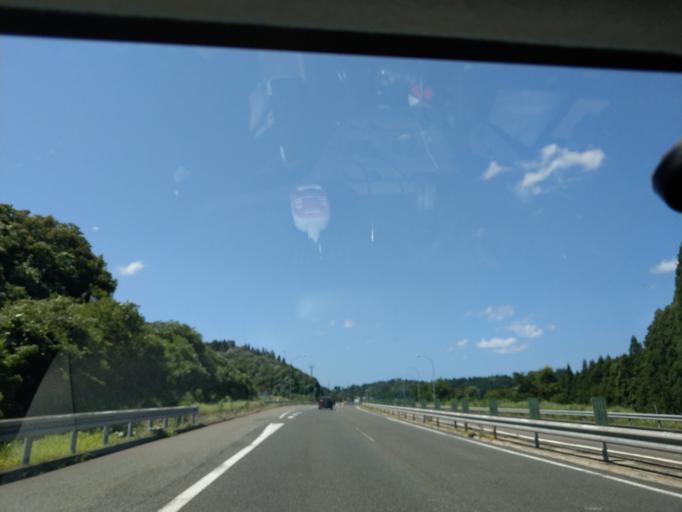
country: JP
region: Akita
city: Akita
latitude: 39.6571
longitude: 140.1955
